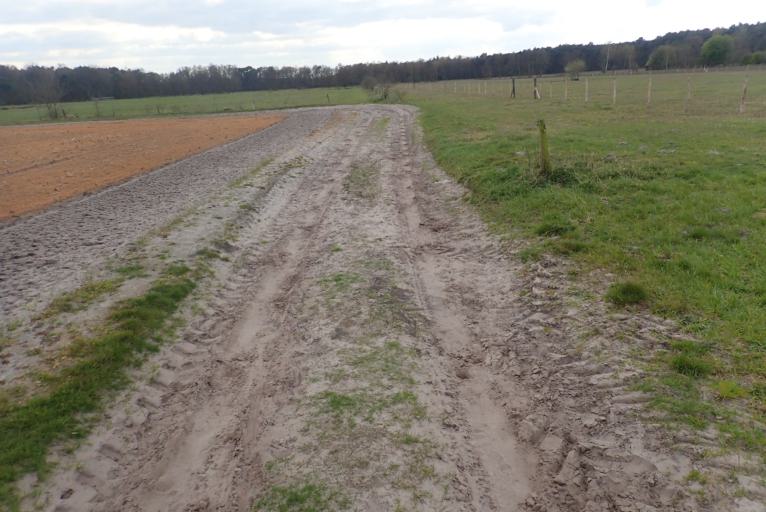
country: BE
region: Flanders
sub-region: Provincie Antwerpen
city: Stabroek
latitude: 51.4127
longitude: 4.3941
